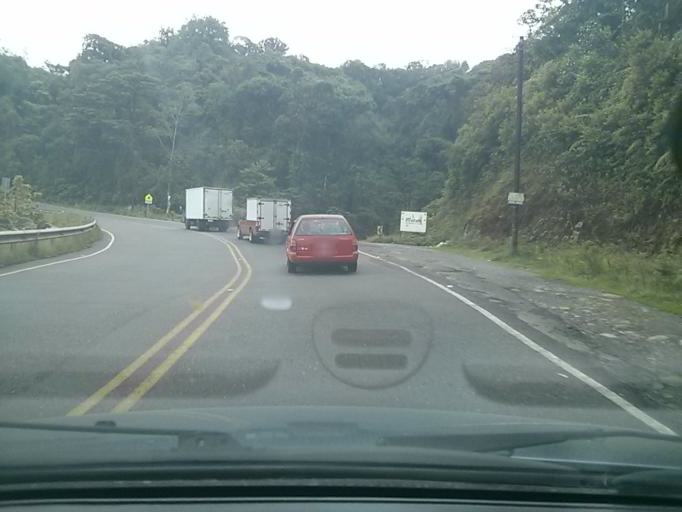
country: CR
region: San Jose
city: San Marcos
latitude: 9.7408
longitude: -83.9615
